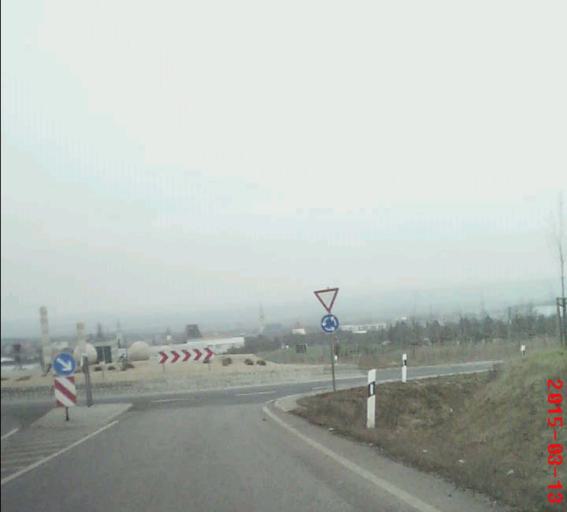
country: DE
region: Thuringia
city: Bad Langensalza
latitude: 51.0912
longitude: 10.6426
